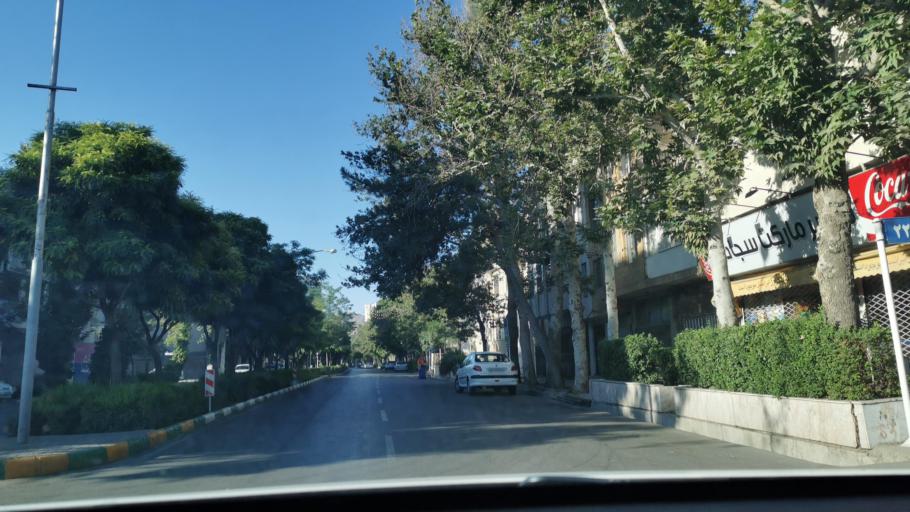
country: IR
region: Razavi Khorasan
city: Mashhad
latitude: 36.2912
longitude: 59.5674
